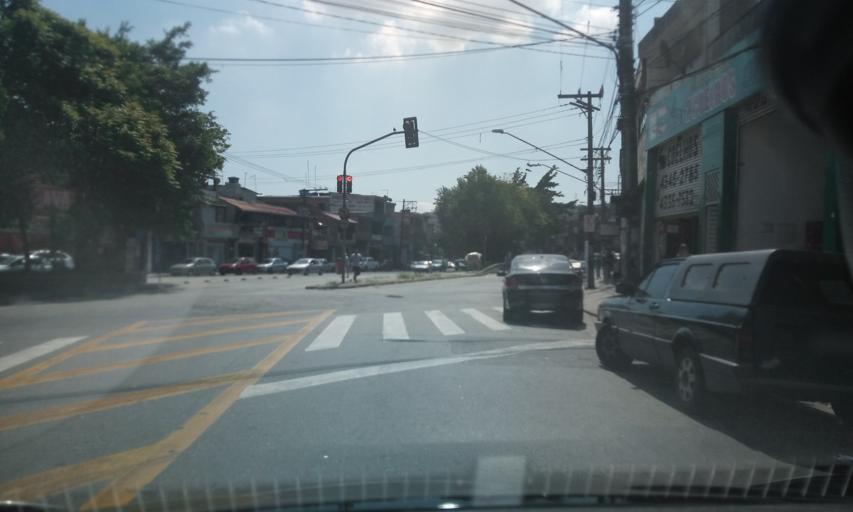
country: BR
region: Sao Paulo
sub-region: Sao Bernardo Do Campo
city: Sao Bernardo do Campo
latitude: -23.7128
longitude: -46.5303
